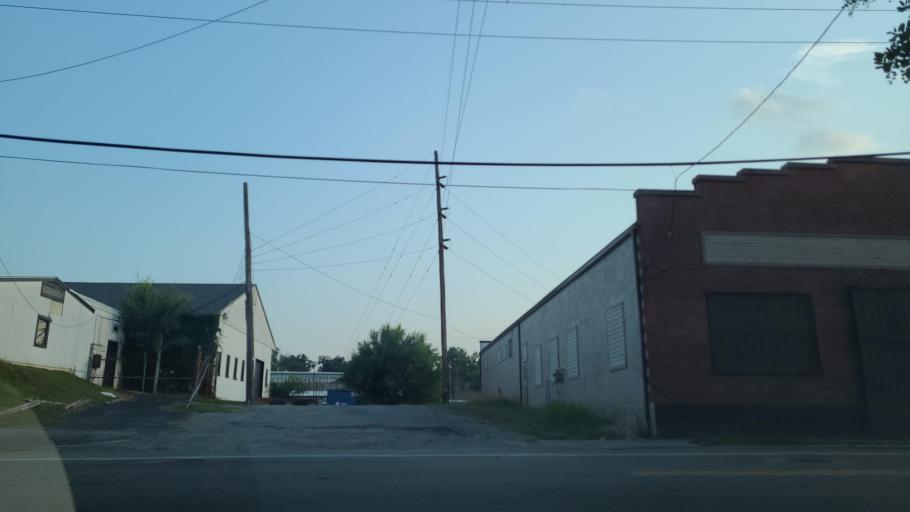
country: US
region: Virginia
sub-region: City of Roanoke
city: Roanoke
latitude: 37.2764
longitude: -79.9550
